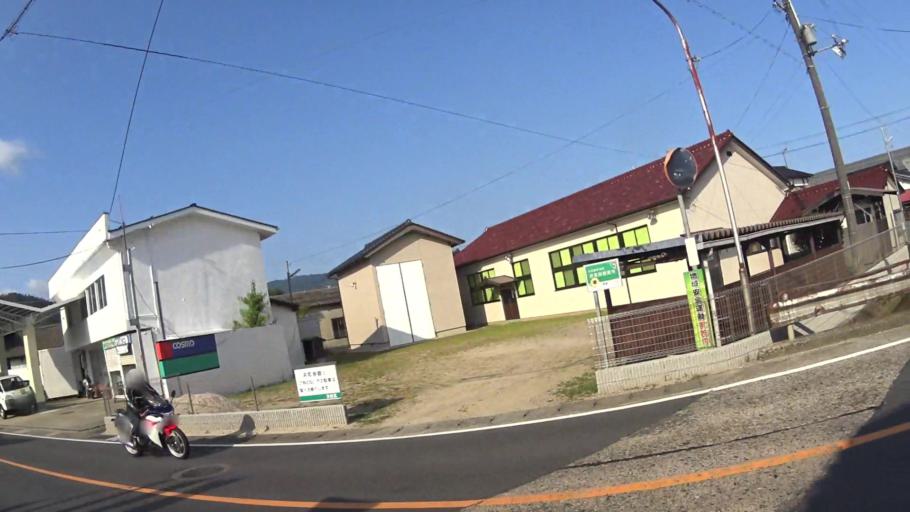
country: JP
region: Kyoto
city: Miyazu
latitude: 35.5636
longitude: 135.1524
